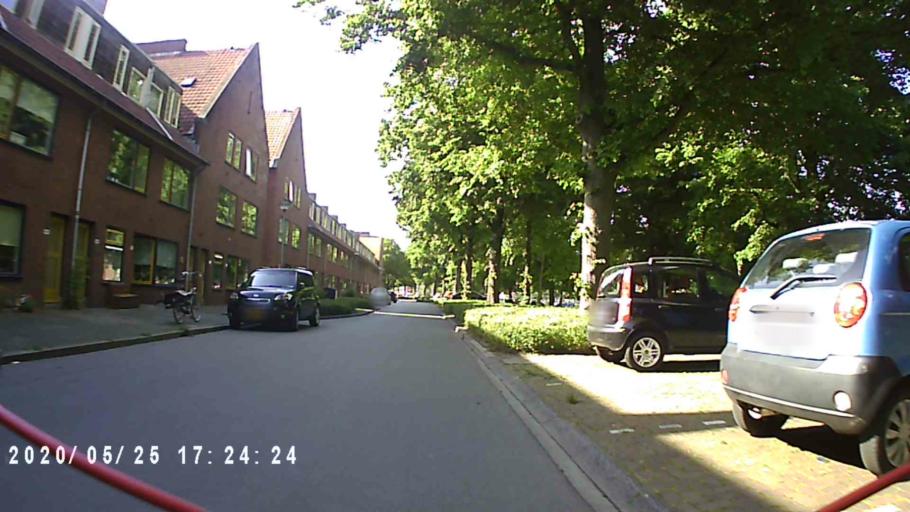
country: NL
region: Groningen
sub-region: Gemeente Groningen
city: Oosterpark
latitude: 53.2283
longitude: 6.5852
